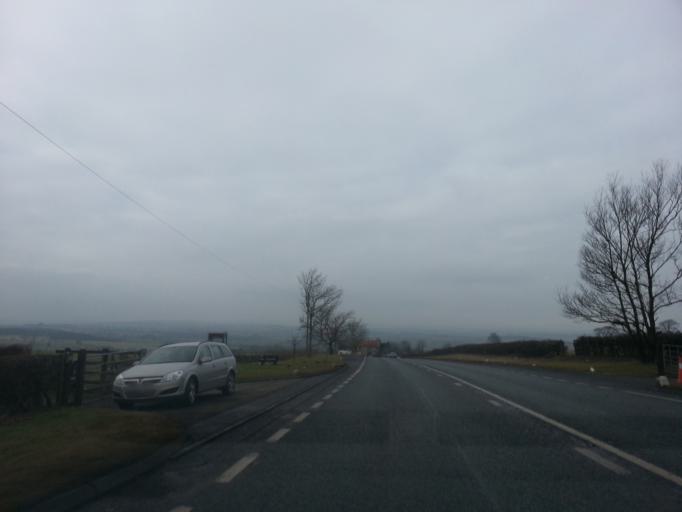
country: GB
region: England
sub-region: County Durham
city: Bishop Auckland
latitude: 54.6132
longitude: -1.6901
